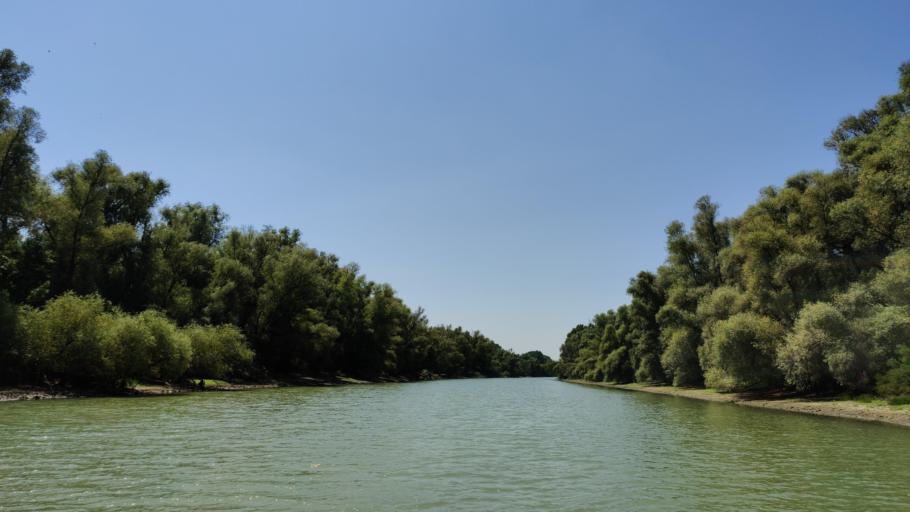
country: RO
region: Tulcea
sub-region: Comuna Nufaru
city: Nufaru
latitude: 45.2229
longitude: 28.8830
